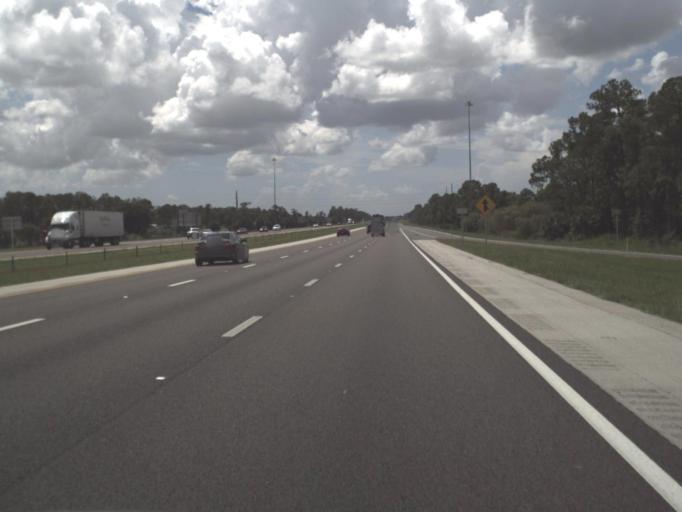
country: US
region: Florida
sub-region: Collier County
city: Vineyards
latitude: 26.2078
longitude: -81.7363
